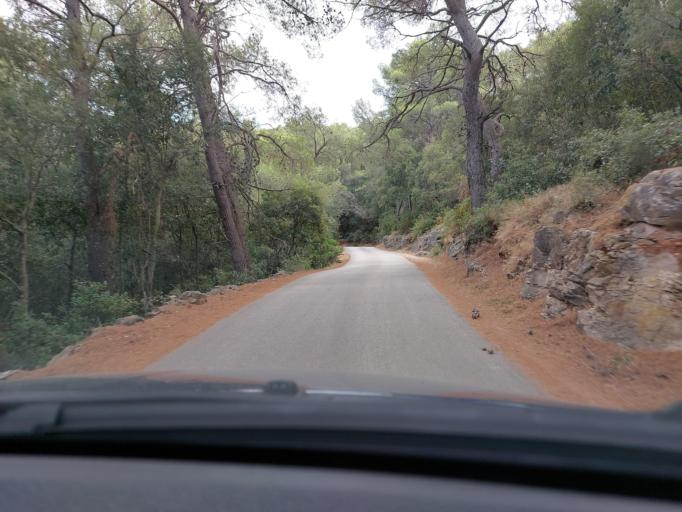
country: HR
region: Dubrovacko-Neretvanska
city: Smokvica
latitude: 42.7626
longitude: 16.9094
